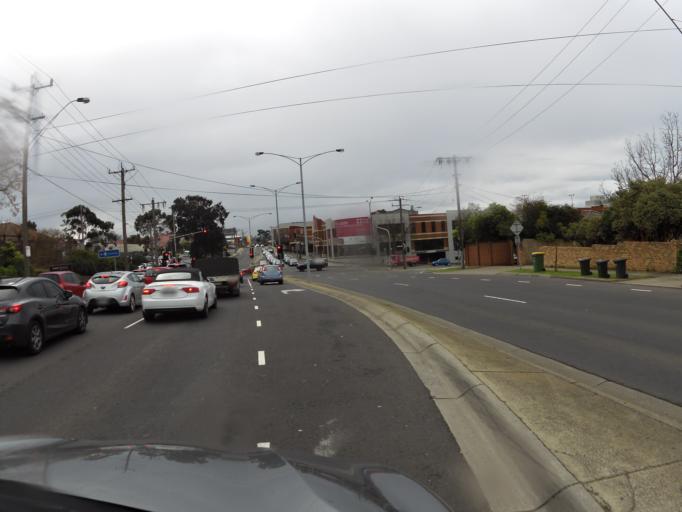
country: AU
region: Victoria
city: Rosanna
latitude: -37.7605
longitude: 145.0688
